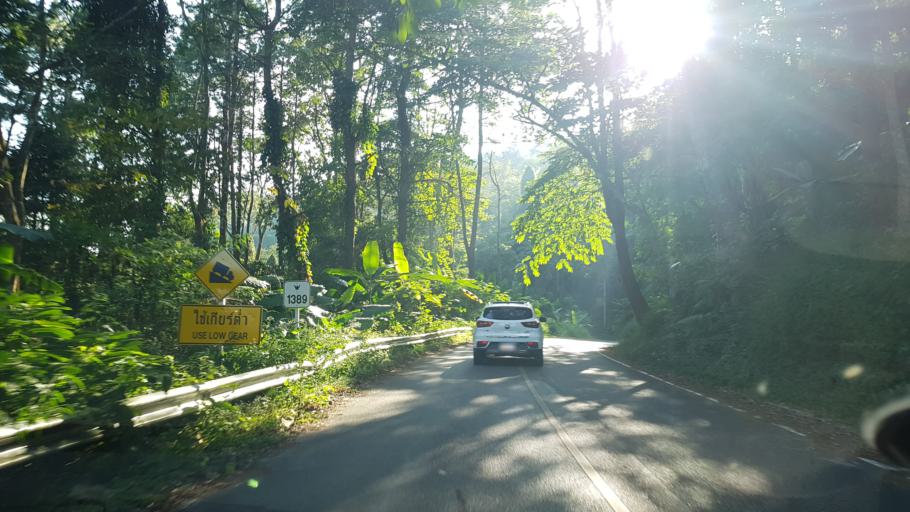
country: TH
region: Chiang Rai
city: Mae Fa Luang
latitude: 20.3273
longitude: 99.8245
